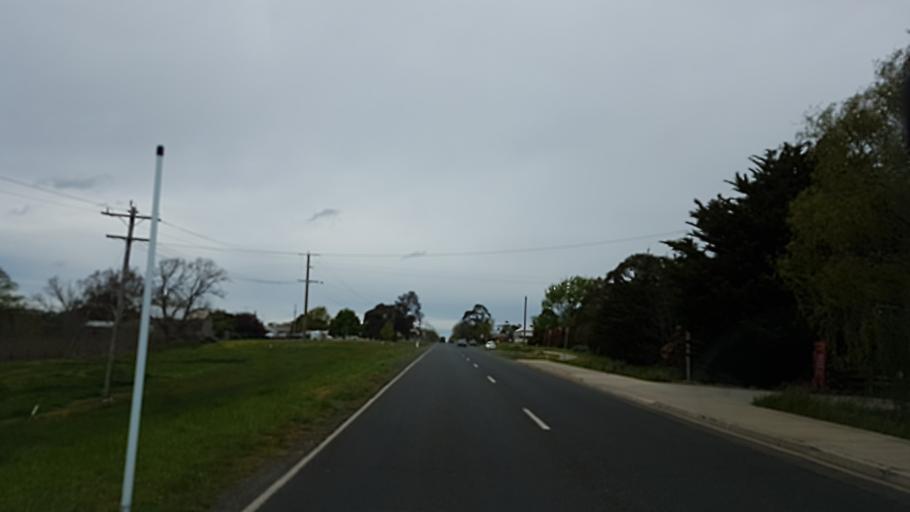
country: AU
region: Victoria
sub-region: Moorabool
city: Bacchus Marsh
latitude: -37.6001
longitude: 144.2171
